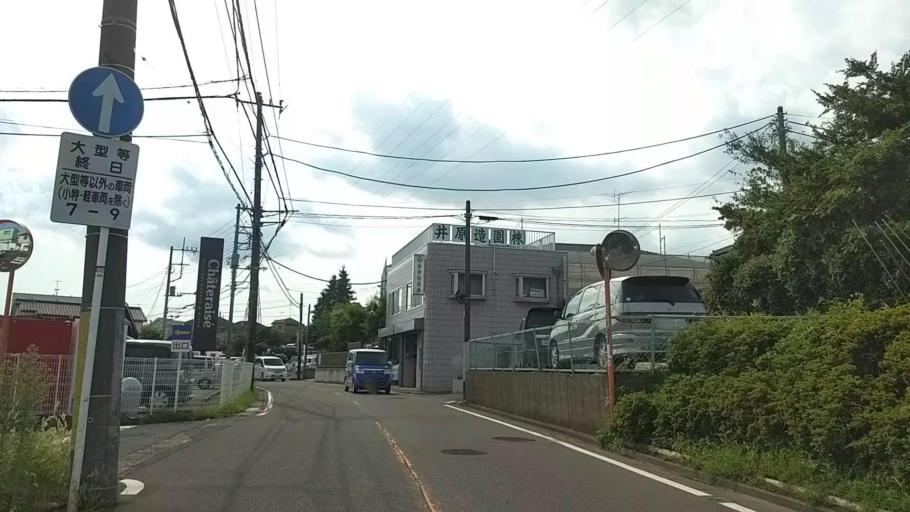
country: JP
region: Kanagawa
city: Yokohama
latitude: 35.4890
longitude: 139.5754
